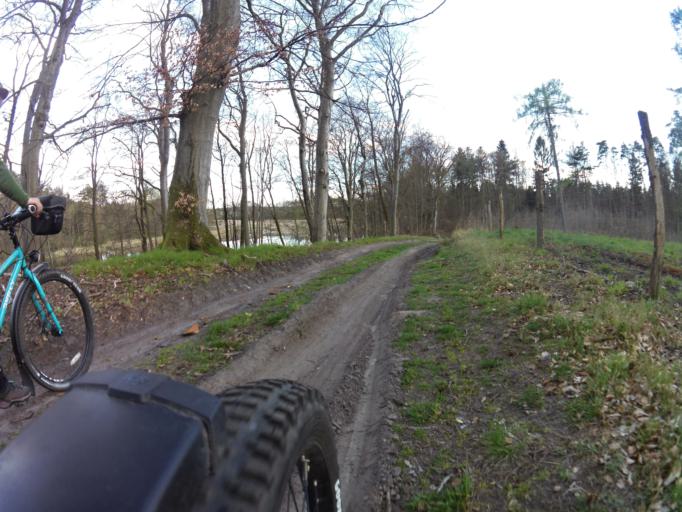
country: PL
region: West Pomeranian Voivodeship
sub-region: Powiat gryficki
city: Ploty
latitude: 53.7561
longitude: 15.2695
